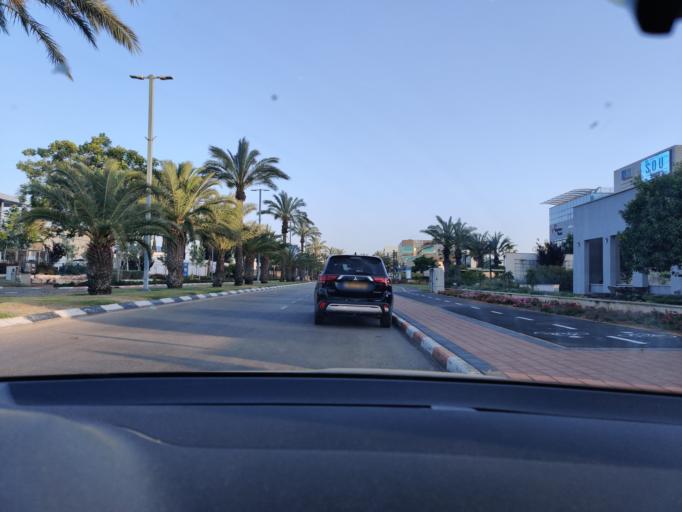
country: IL
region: Haifa
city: Qesarya
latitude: 32.4857
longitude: 34.9479
